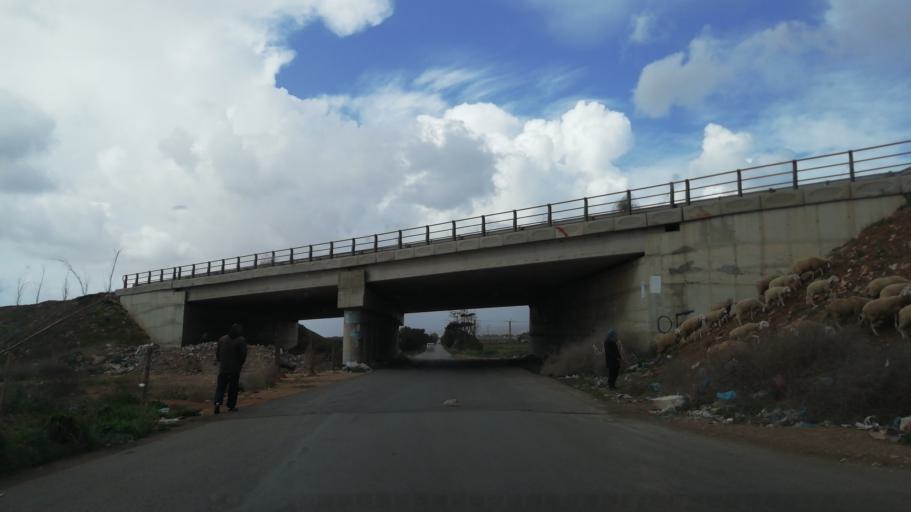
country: DZ
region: Oran
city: Sidi ech Chahmi
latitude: 35.6226
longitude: -0.5509
